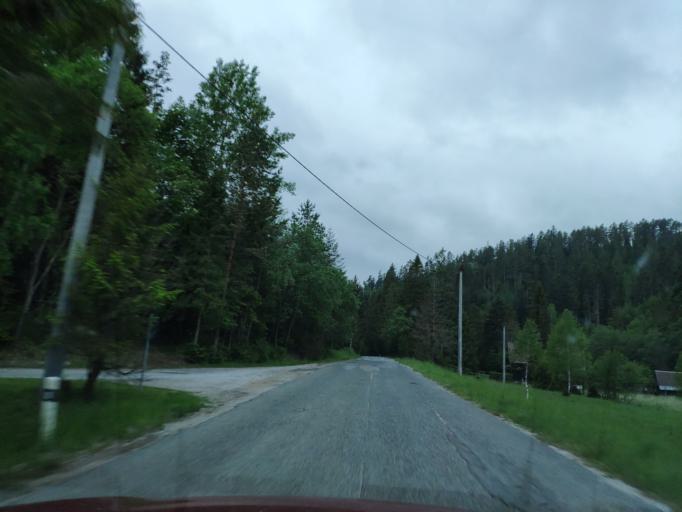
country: SK
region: Kosicky
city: Roznava
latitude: 48.7135
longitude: 20.7052
